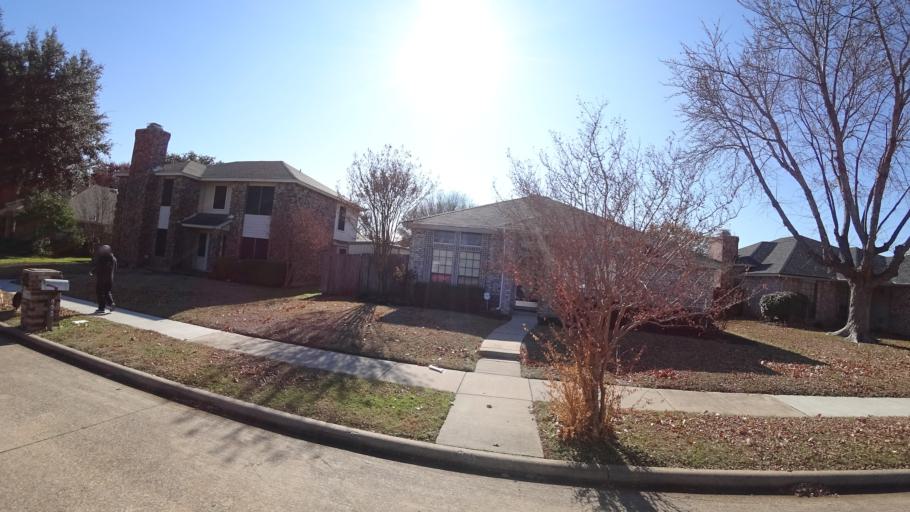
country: US
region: Texas
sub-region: Denton County
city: Lewisville
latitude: 33.0094
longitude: -97.0140
